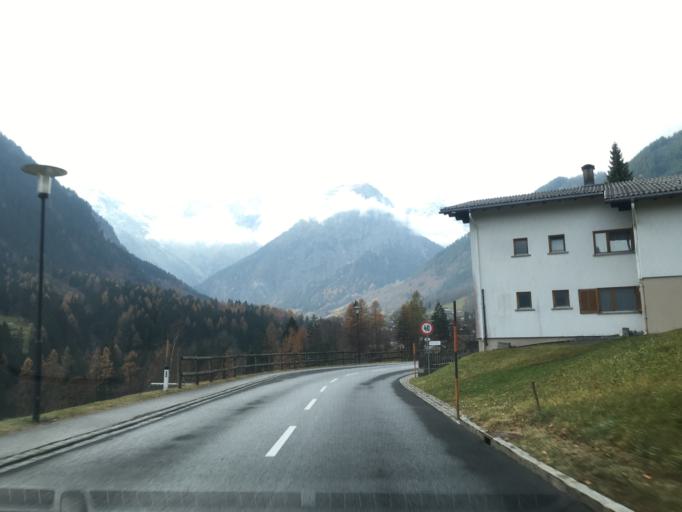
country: AT
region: Vorarlberg
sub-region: Politischer Bezirk Bludenz
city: Brand
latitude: 47.1175
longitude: 9.7524
